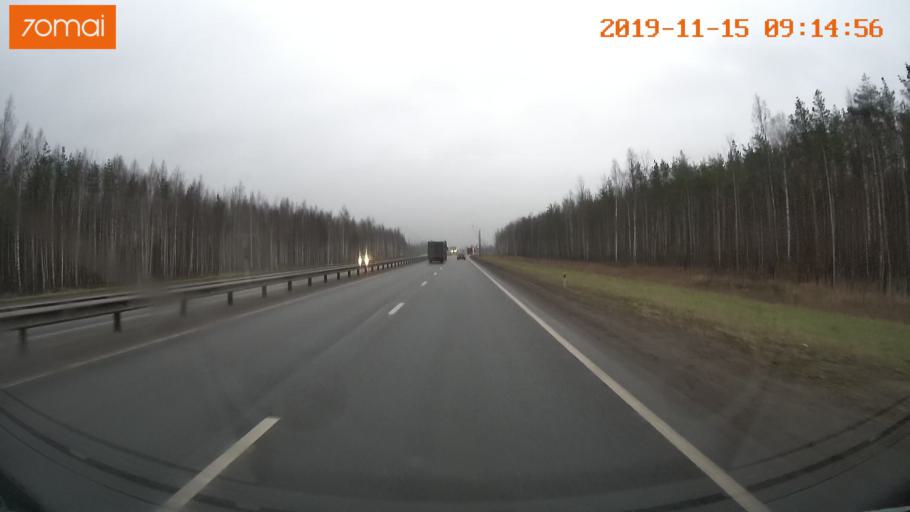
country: RU
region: Vologda
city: Tonshalovo
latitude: 59.2328
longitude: 37.9631
